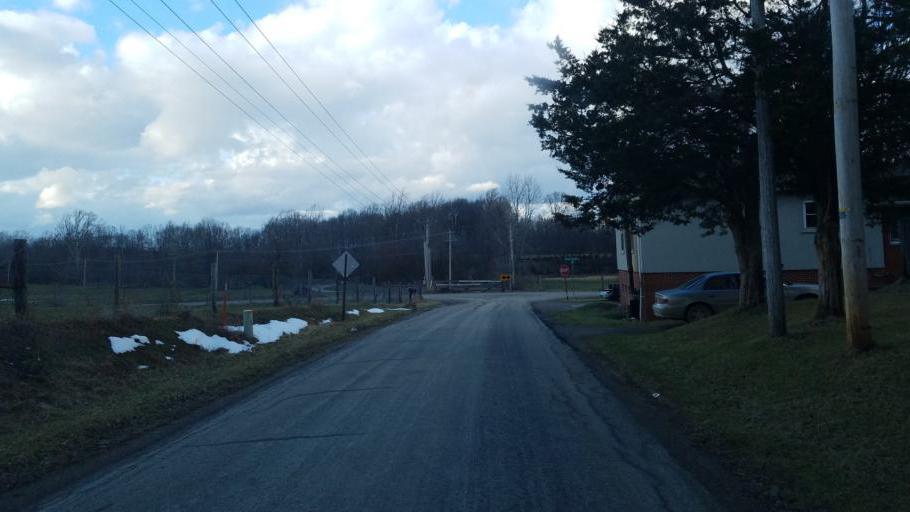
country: US
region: Ohio
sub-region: Richland County
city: Lexington
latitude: 40.6187
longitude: -82.6062
